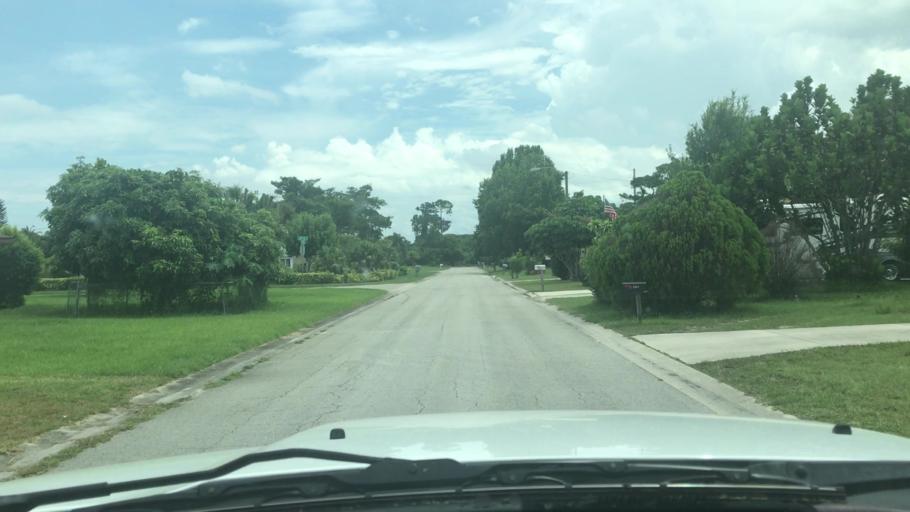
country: US
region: Florida
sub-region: Indian River County
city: Florida Ridge
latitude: 27.5602
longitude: -80.3889
